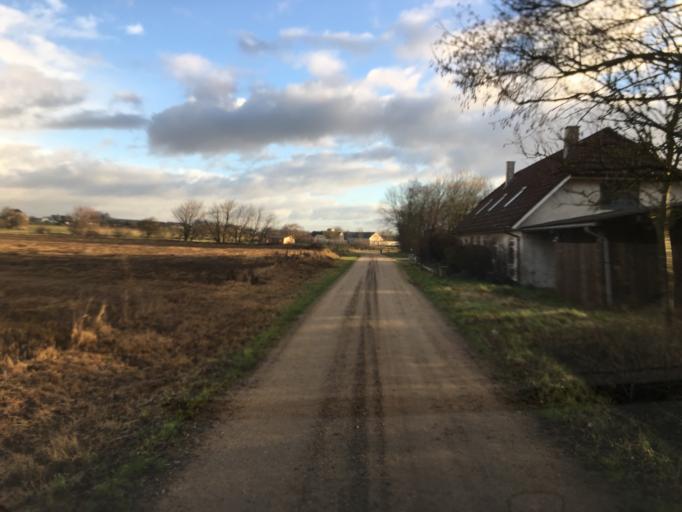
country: DK
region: South Denmark
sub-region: Tonder Kommune
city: Sherrebek
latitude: 55.1537
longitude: 8.8184
